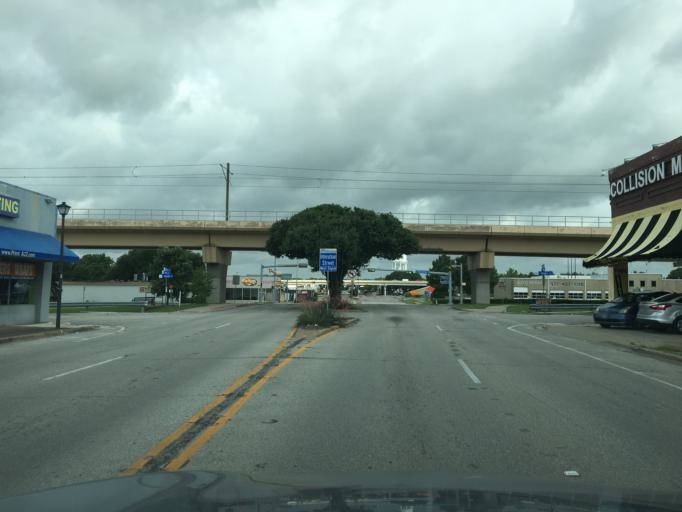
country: US
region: Texas
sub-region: Dallas County
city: Richardson
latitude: 32.9490
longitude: -96.7314
